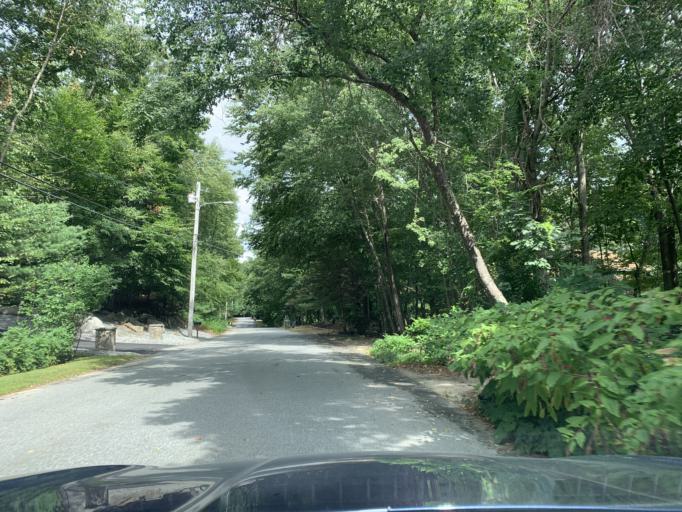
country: US
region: Rhode Island
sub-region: Kent County
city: West Warwick
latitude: 41.7372
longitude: -71.5850
